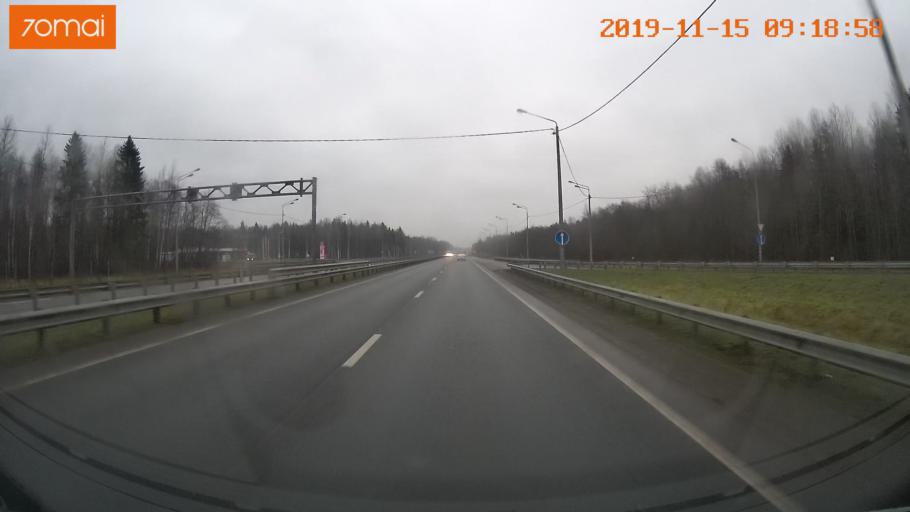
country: RU
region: Vologda
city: Tonshalovo
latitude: 59.2797
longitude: 38.0069
